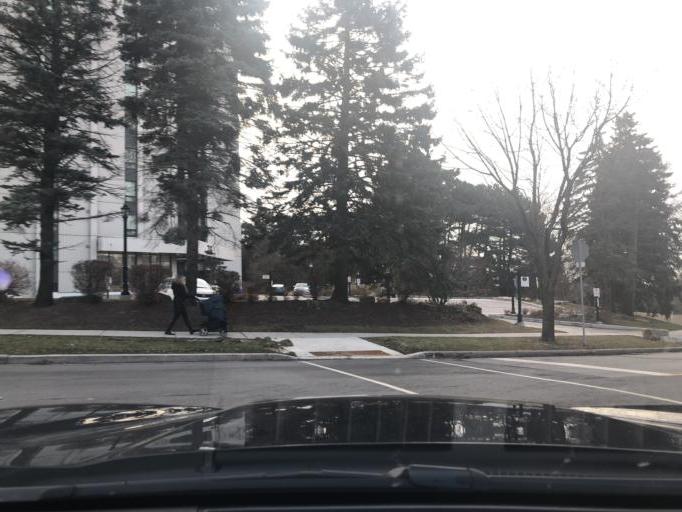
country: CA
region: Ontario
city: Willowdale
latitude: 43.7648
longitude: -79.3448
